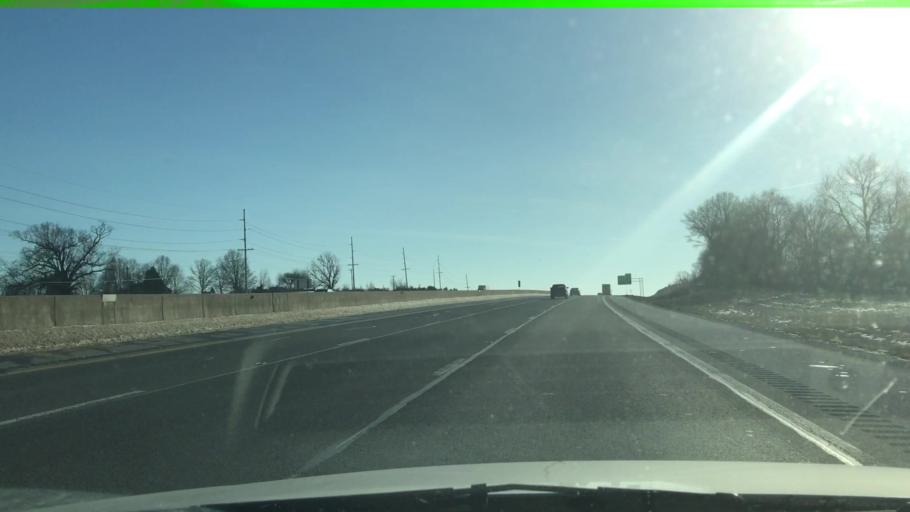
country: US
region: Kentucky
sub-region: Warren County
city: Bowling Green
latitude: 36.9666
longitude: -86.3971
